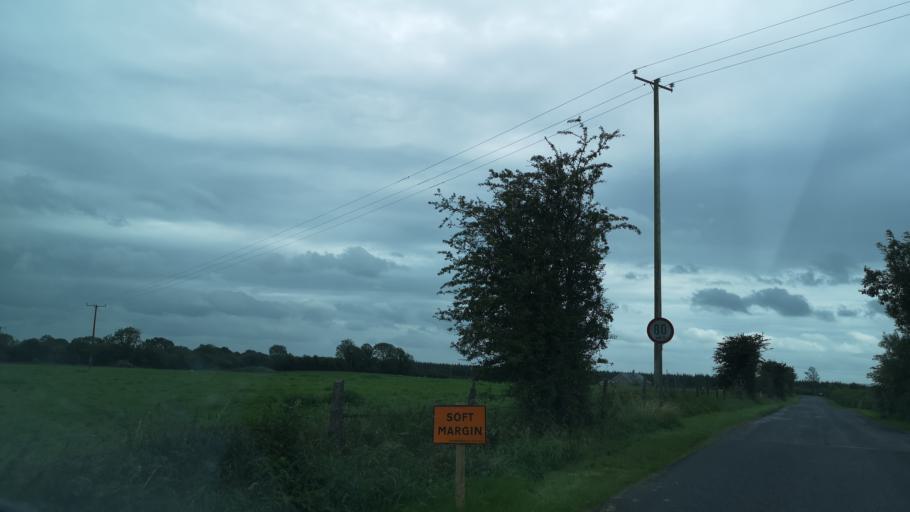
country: IE
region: Leinster
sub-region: Uibh Fhaili
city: Ferbane
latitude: 53.2345
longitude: -7.7318
